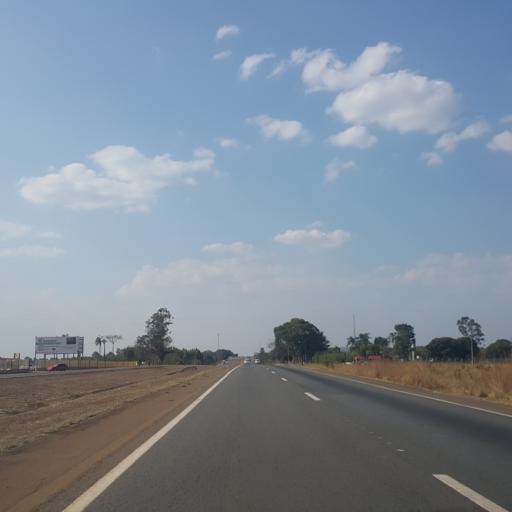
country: BR
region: Goias
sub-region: Abadiania
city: Abadiania
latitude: -16.2361
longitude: -48.7586
